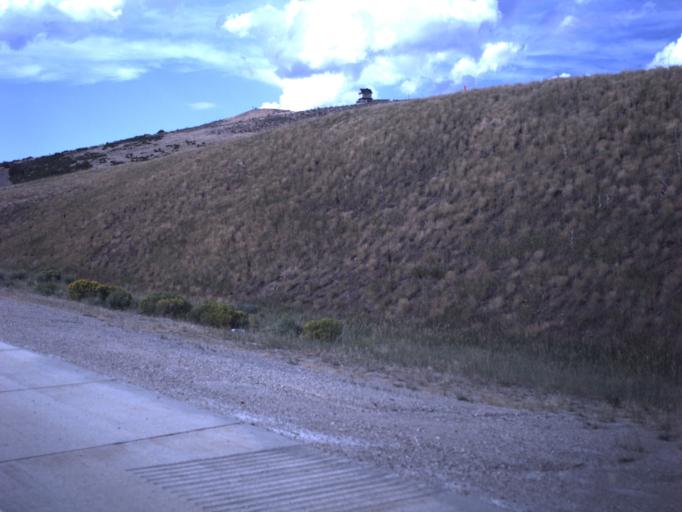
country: US
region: Utah
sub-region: Summit County
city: Park City
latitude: 40.6484
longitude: -111.4551
